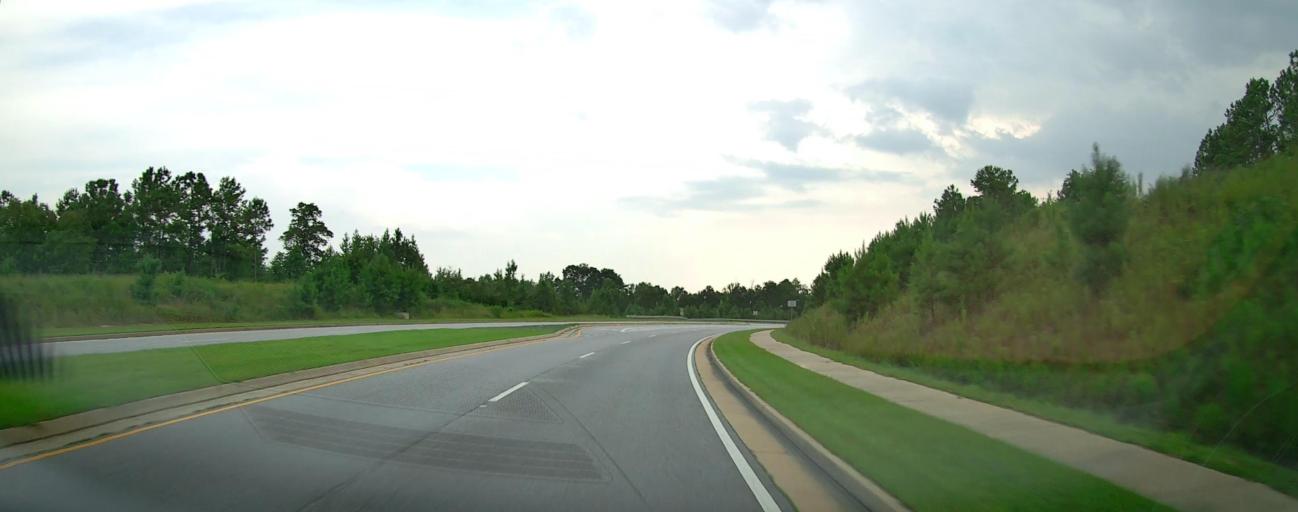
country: US
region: Georgia
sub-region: Muscogee County
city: Columbus
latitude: 32.4906
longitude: -84.8571
